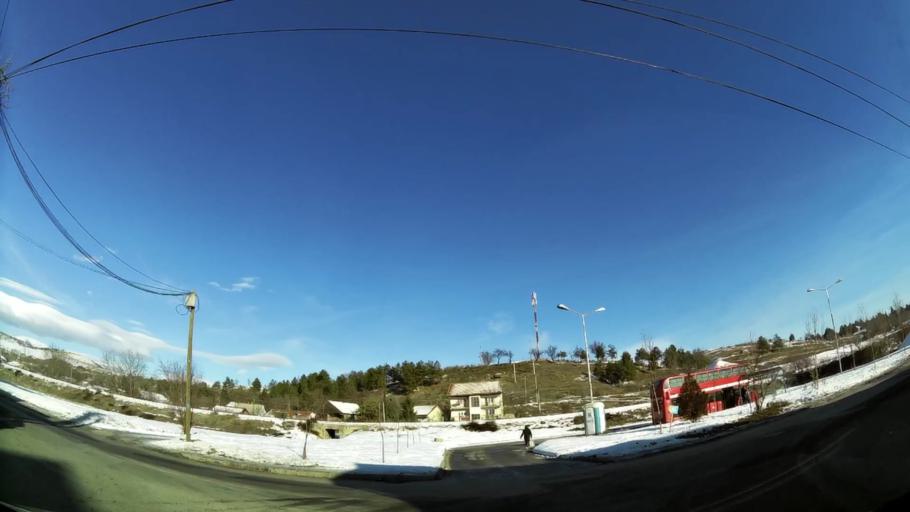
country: MK
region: Saraj
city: Saraj
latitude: 42.0102
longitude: 21.3397
